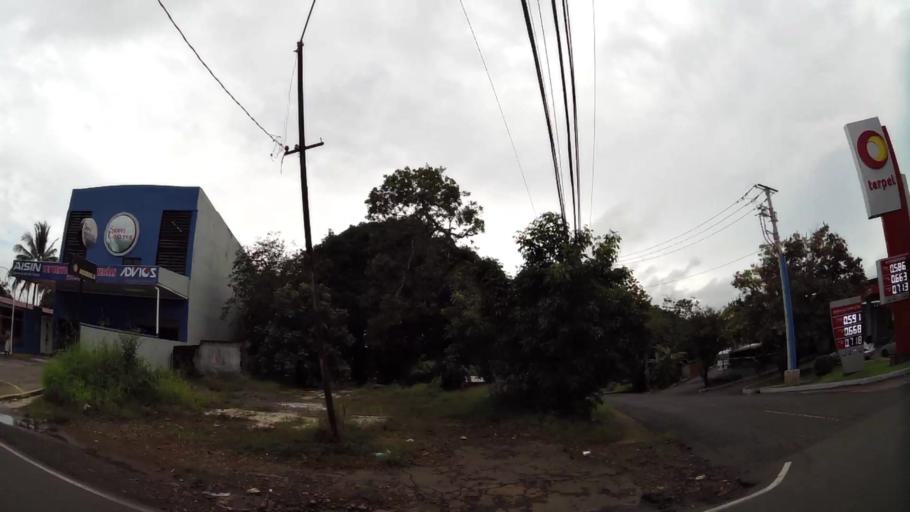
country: PA
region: Chiriqui
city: David
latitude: 8.4384
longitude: -82.4220
